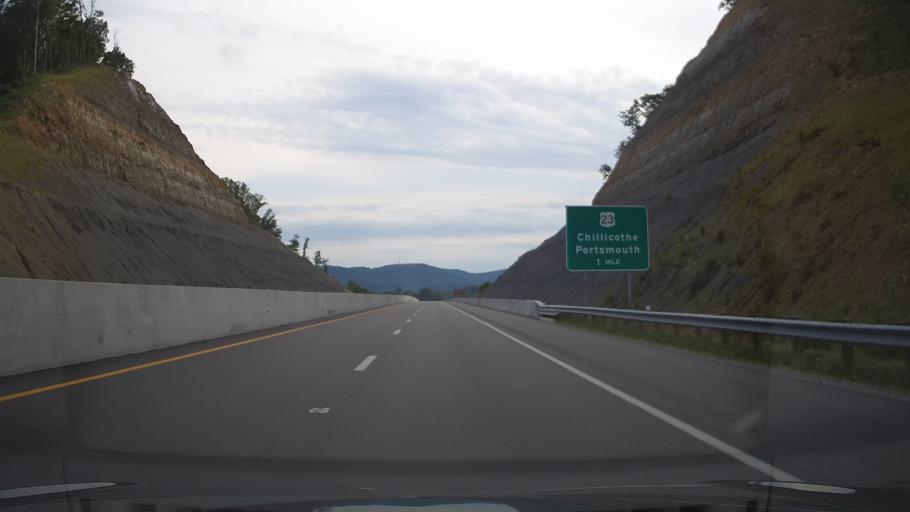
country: US
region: Ohio
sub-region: Scioto County
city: Lucasville
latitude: 38.8961
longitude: -82.9758
